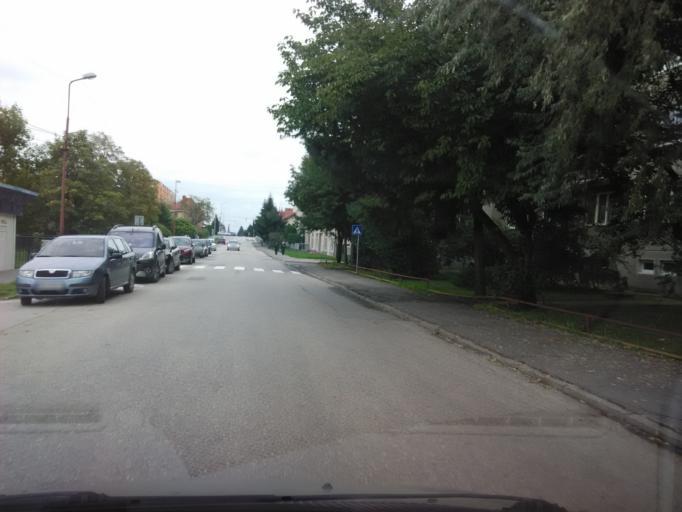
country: SK
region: Nitriansky
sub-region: Okres Nitra
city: Vrable
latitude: 48.2419
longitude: 18.3079
